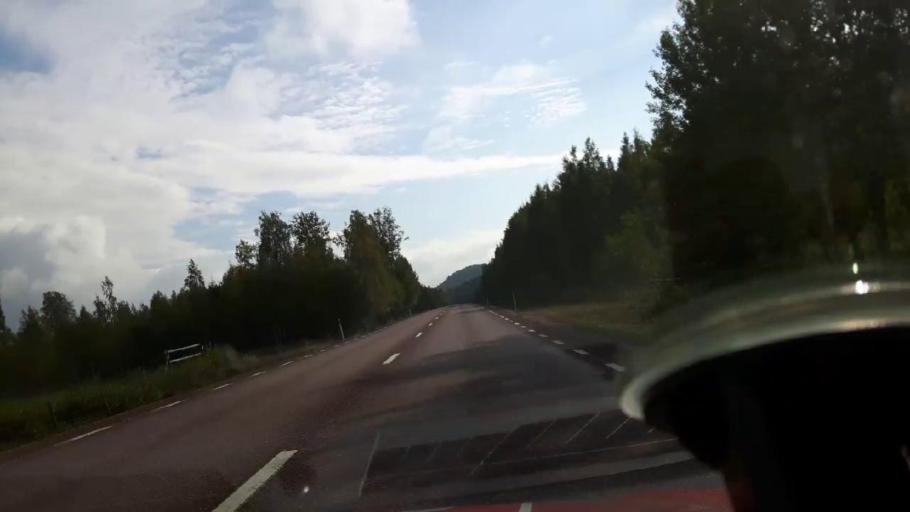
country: SE
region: Gaevleborg
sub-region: Bollnas Kommun
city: Kilafors
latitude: 61.2143
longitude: 16.7351
